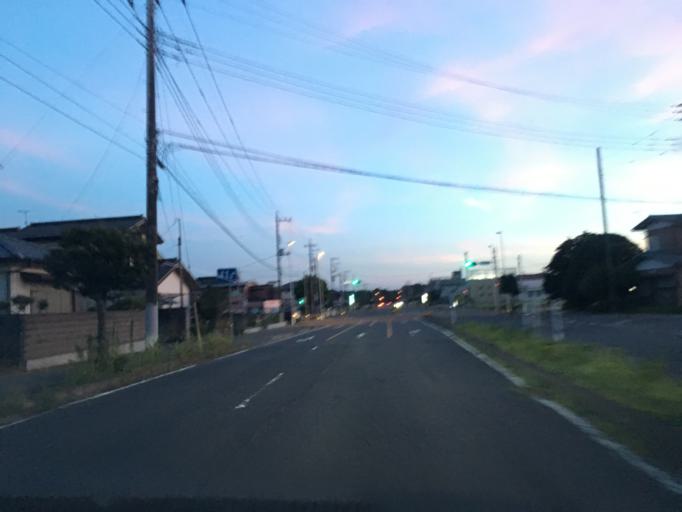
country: JP
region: Ibaraki
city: Hitachi-Naka
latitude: 36.3927
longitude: 140.5547
